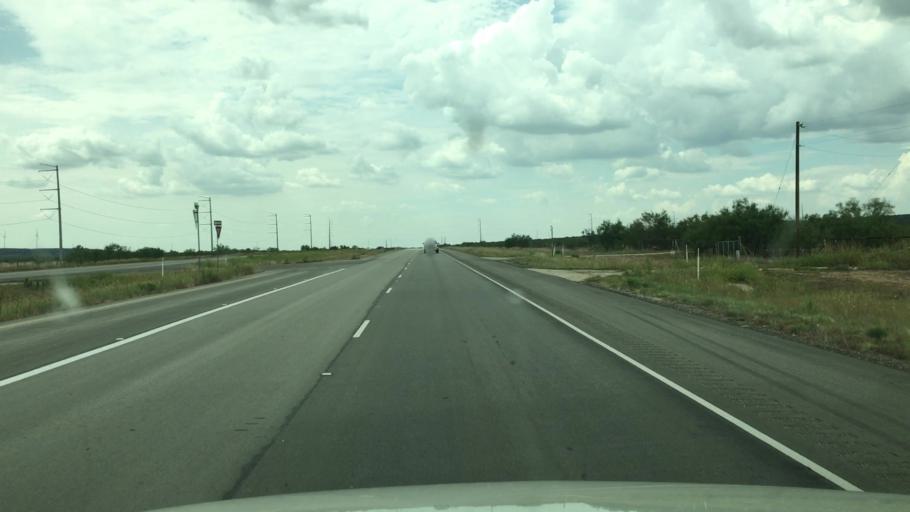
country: US
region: Texas
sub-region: Glasscock County
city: Garden City
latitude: 31.9798
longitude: -101.2536
